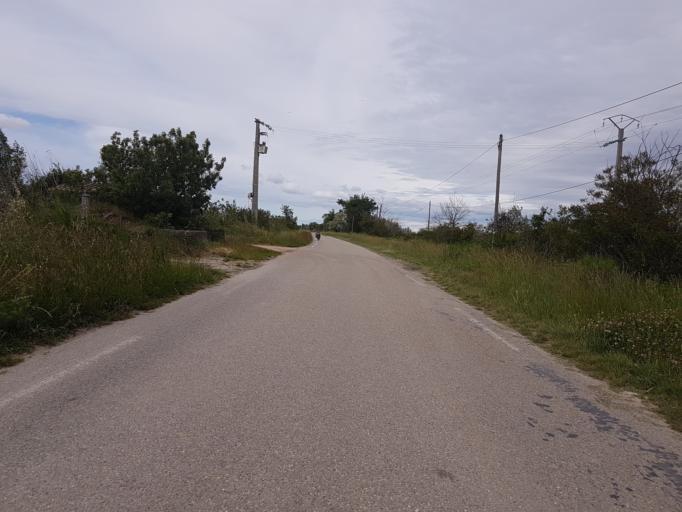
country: FR
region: Languedoc-Roussillon
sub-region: Departement du Gard
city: Saint-Gilles
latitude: 43.6050
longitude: 4.3676
